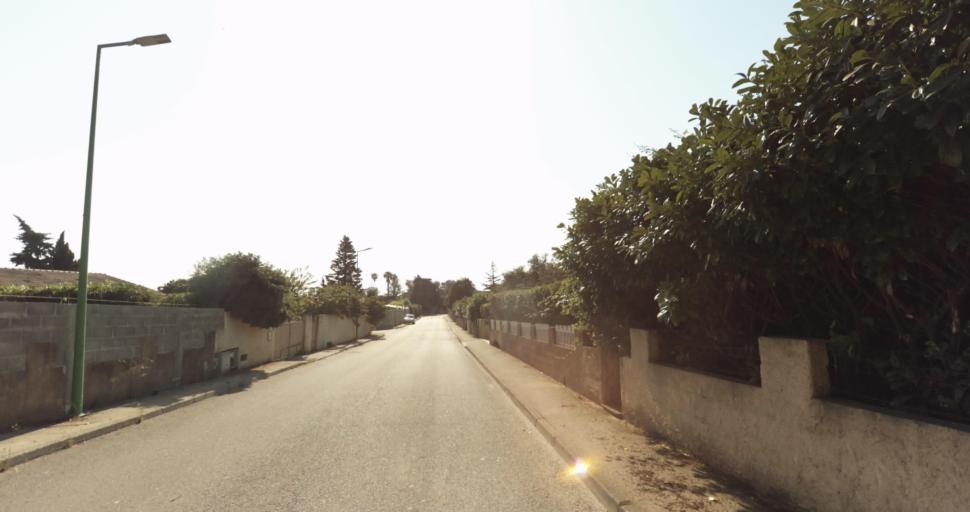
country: FR
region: Corsica
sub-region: Departement de la Haute-Corse
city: Biguglia
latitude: 42.6381
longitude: 9.4308
